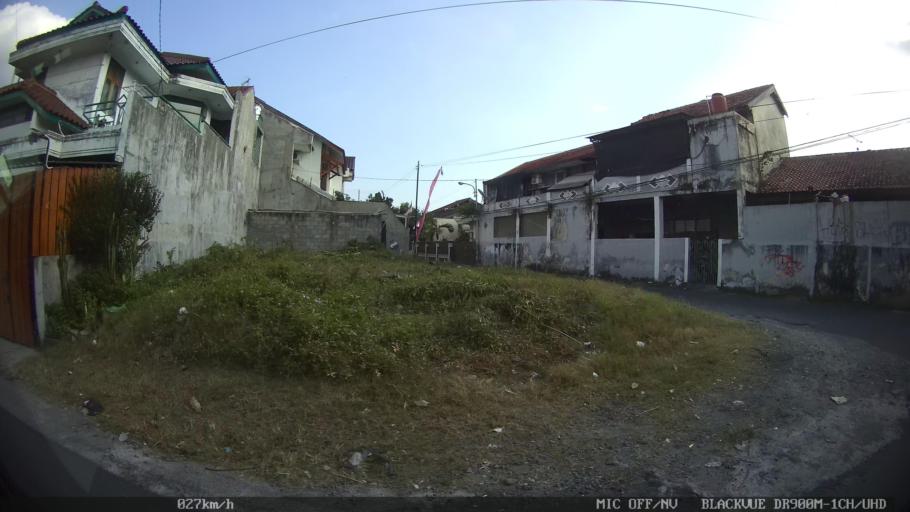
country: ID
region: Daerah Istimewa Yogyakarta
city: Yogyakarta
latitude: -7.7894
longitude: 110.3527
